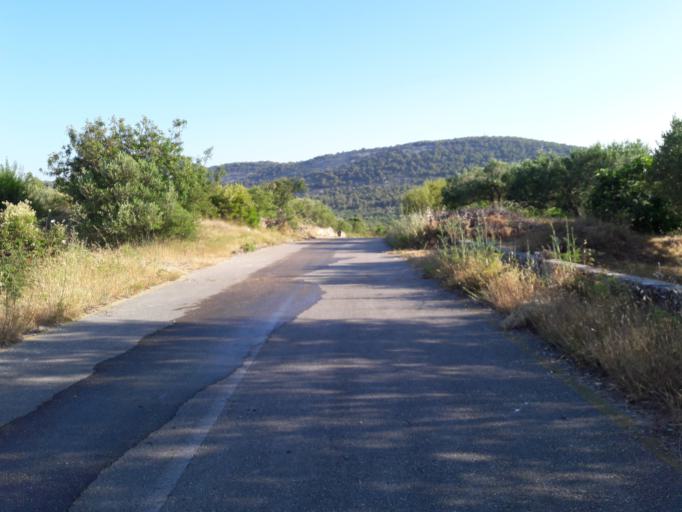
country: HR
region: Sibensko-Kniniska
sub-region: Grad Sibenik
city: Sibenik
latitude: 43.6984
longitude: 15.8476
